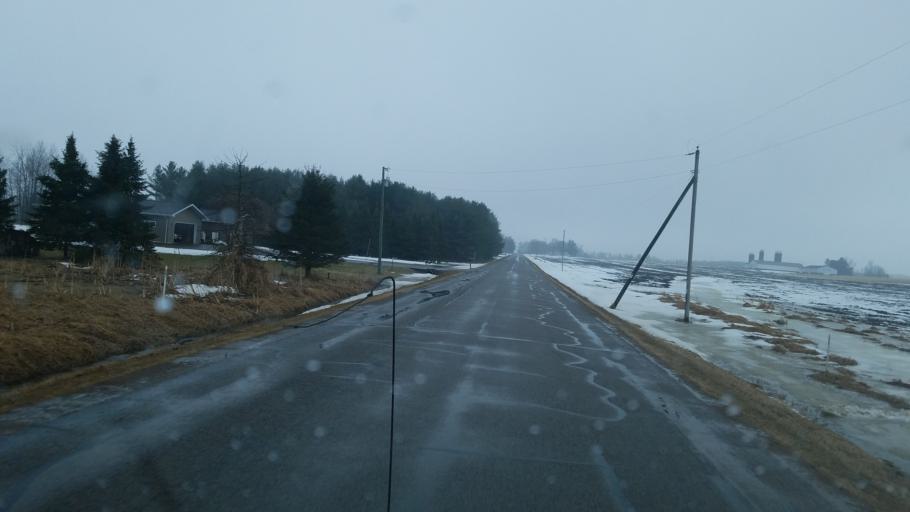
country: US
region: Wisconsin
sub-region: Marathon County
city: Spencer
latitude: 44.6636
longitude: -90.2791
